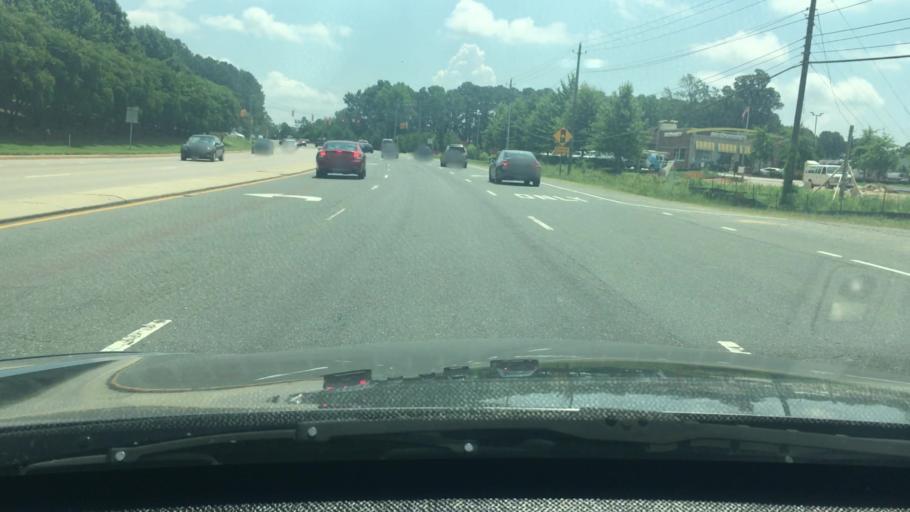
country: US
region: North Carolina
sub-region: Wake County
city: Cary
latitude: 35.7908
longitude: -78.7420
